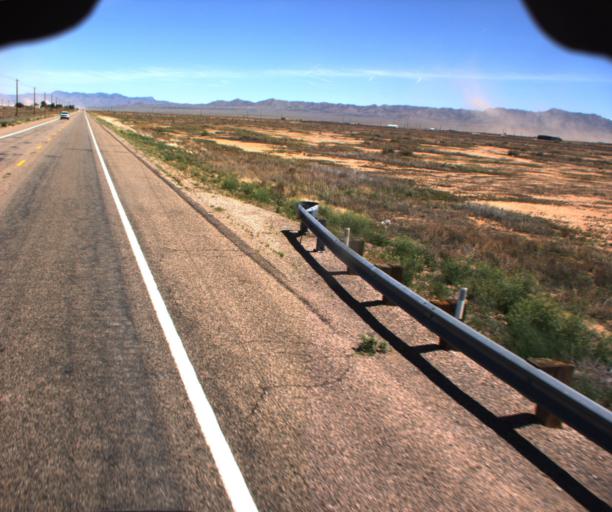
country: US
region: Arizona
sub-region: Mohave County
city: New Kingman-Butler
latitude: 35.2788
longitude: -113.9519
